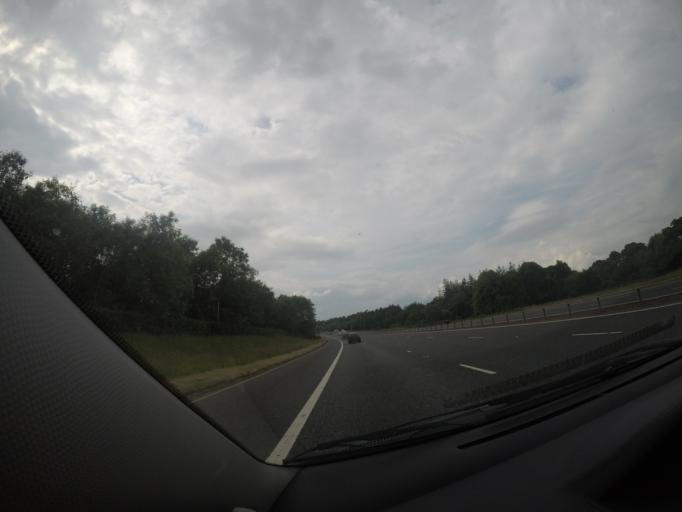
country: GB
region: Scotland
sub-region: Dumfries and Galloway
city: Lockerbie
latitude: 55.0943
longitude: -3.3244
